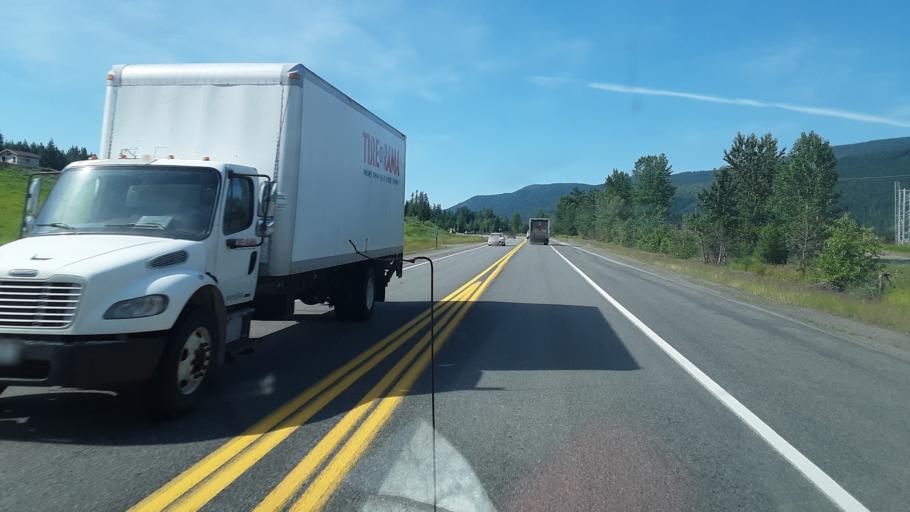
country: US
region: Idaho
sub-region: Bonner County
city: Ponderay
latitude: 48.4067
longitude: -116.5269
